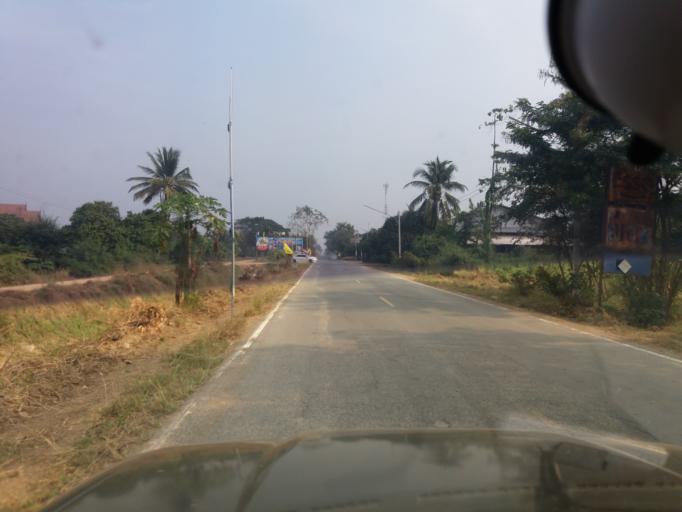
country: TH
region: Suphan Buri
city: Doem Bang Nang Buat
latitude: 14.8705
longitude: 100.1724
